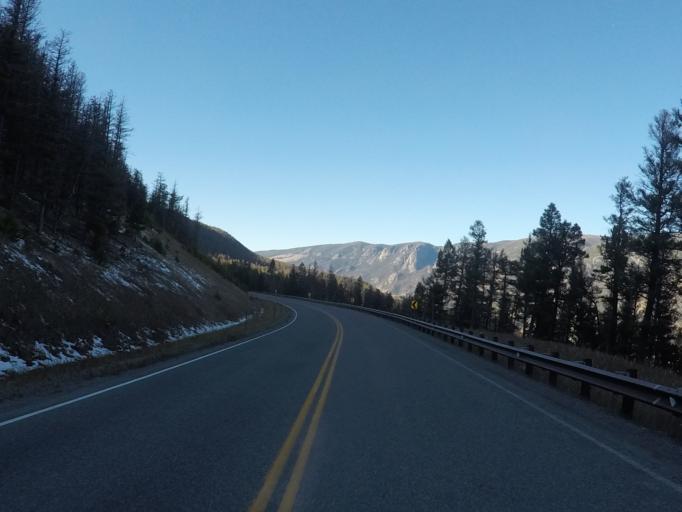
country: US
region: Montana
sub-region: Carbon County
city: Red Lodge
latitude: 44.8113
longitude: -109.4531
